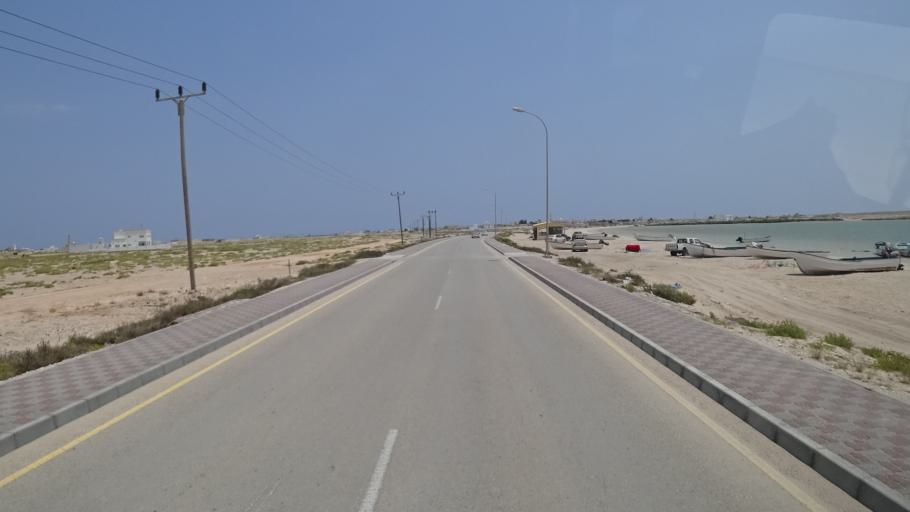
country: OM
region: Ash Sharqiyah
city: Sur
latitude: 22.5284
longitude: 59.7803
